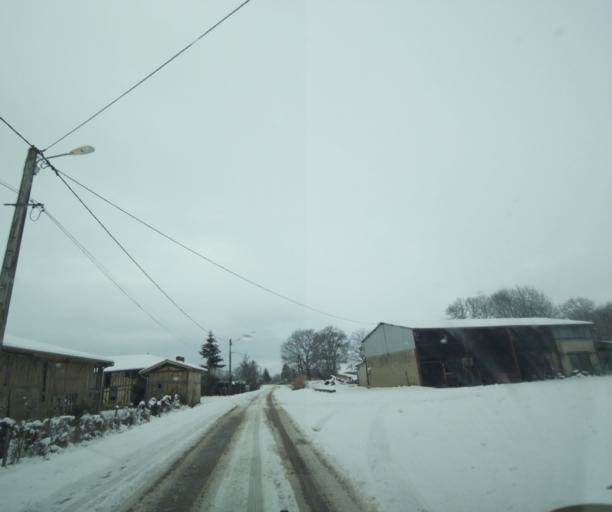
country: FR
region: Champagne-Ardenne
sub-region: Departement de la Haute-Marne
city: Montier-en-Der
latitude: 48.5256
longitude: 4.7215
